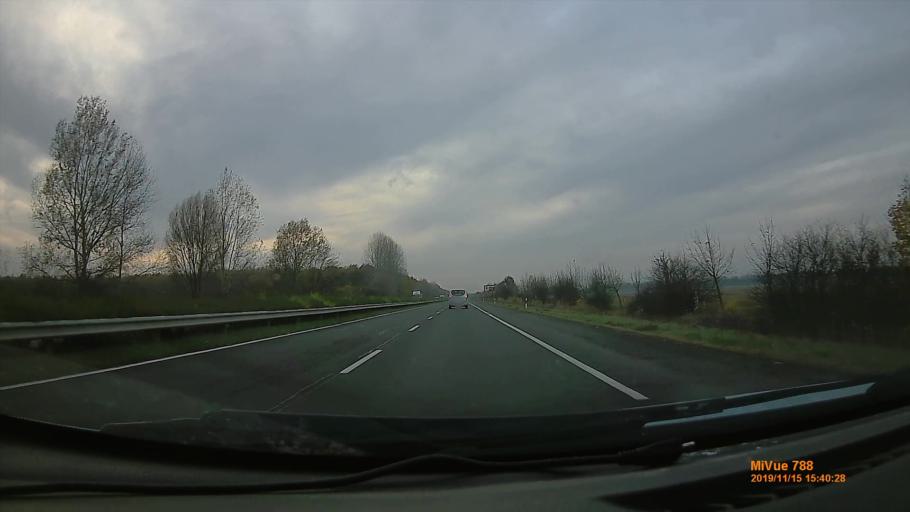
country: HU
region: Bekes
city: Bekescsaba
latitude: 46.6744
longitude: 21.1516
